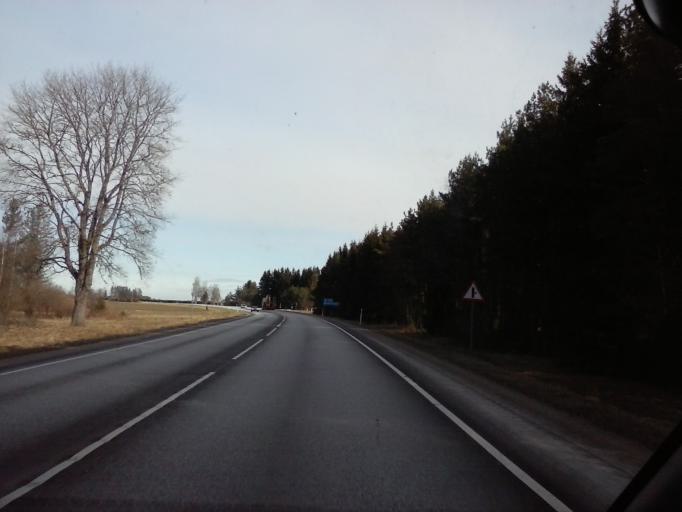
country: EE
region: Jaervamaa
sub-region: Paide linn
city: Paide
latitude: 58.8398
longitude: 25.7412
